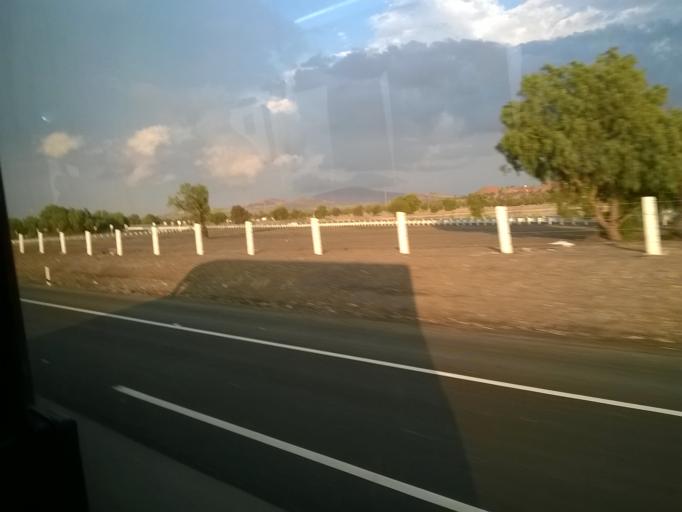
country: MX
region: Mexico
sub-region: Tecamac
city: Fraccionamiento Hacienda del Bosque
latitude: 19.7336
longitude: -98.9497
